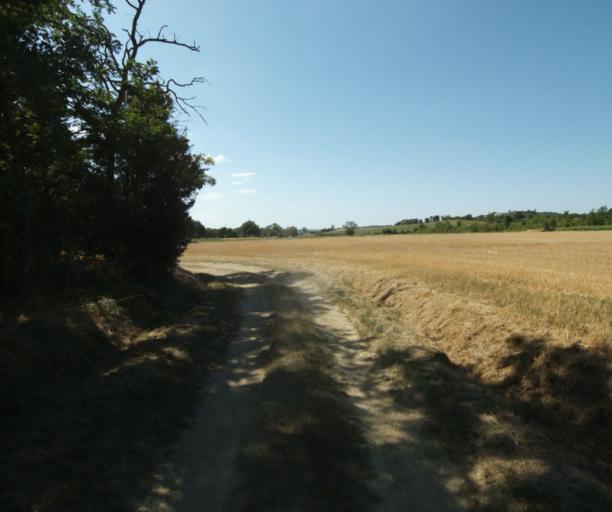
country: FR
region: Midi-Pyrenees
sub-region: Departement de la Haute-Garonne
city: Saint-Felix-Lauragais
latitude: 43.4737
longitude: 1.9074
